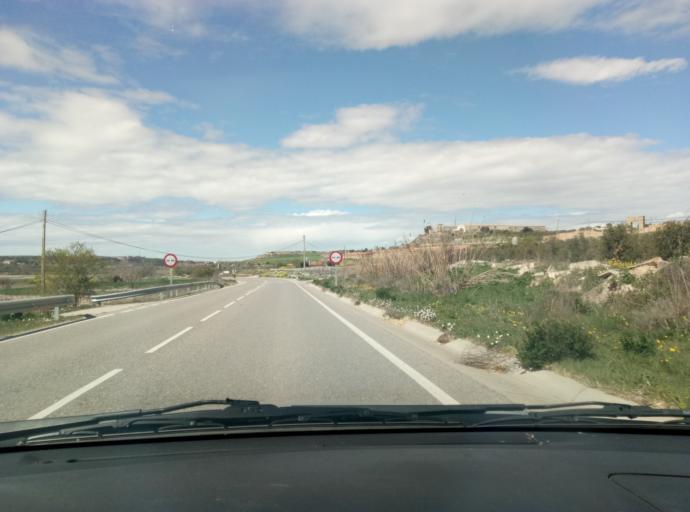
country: ES
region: Catalonia
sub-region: Provincia de Lleida
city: Vallbona de les Monges
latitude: 41.5579
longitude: 1.0498
